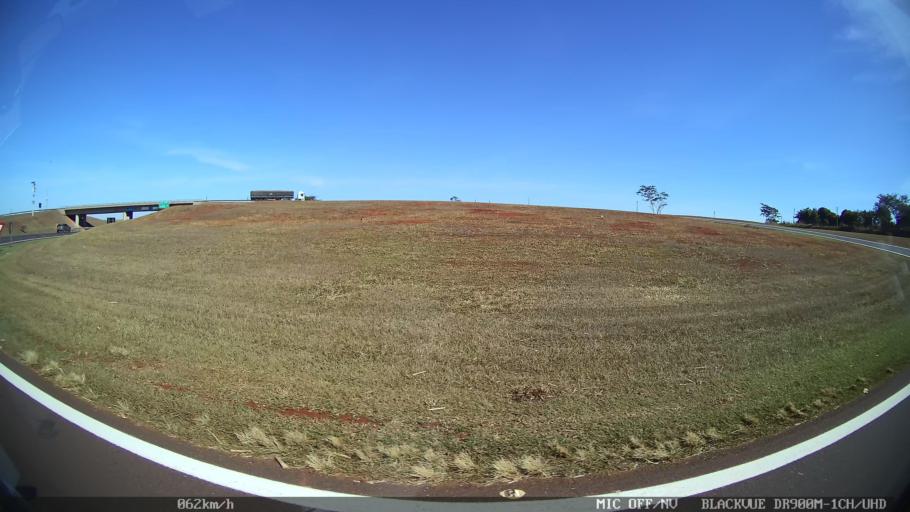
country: BR
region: Sao Paulo
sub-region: Sao Joaquim Da Barra
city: Sao Joaquim da Barra
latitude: -20.5225
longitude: -47.8410
